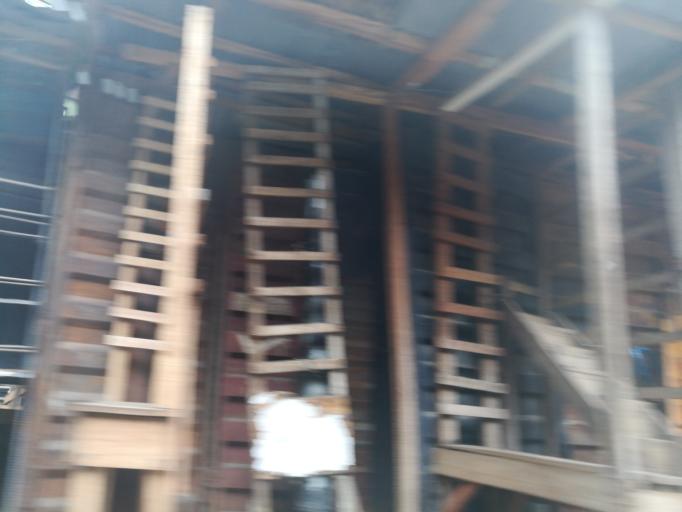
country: NG
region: Lagos
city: Lagos
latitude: 6.4582
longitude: 3.3889
